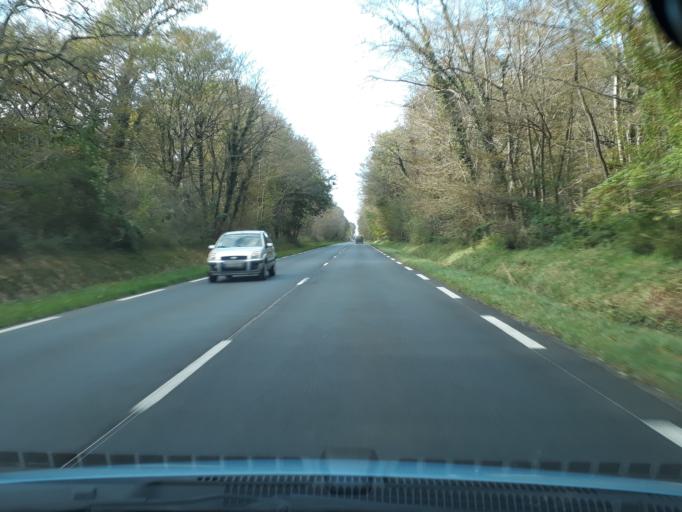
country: FR
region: Ile-de-France
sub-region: Departement de Seine-et-Marne
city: Acheres-la-Foret
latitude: 48.3584
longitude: 2.6231
